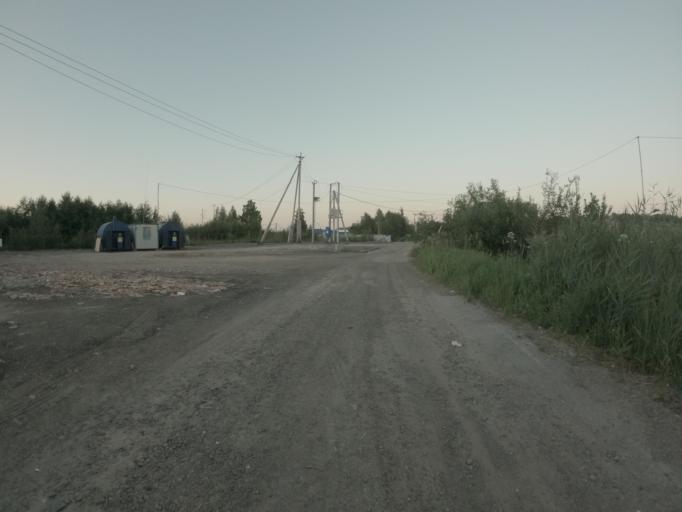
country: RU
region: Leningrad
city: Yanino Vtoroye
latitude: 59.9372
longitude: 30.5490
